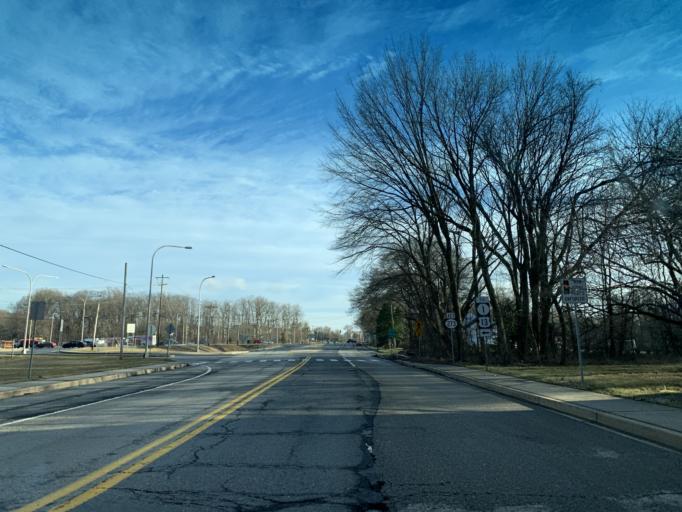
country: US
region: Delaware
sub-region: New Castle County
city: Bear
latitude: 39.6623
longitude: -75.6556
